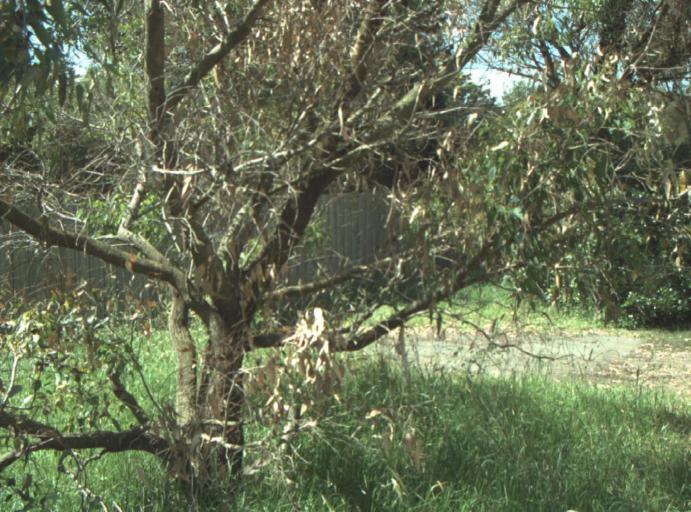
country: AU
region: Victoria
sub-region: Greater Geelong
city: Leopold
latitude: -38.1647
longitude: 144.4730
